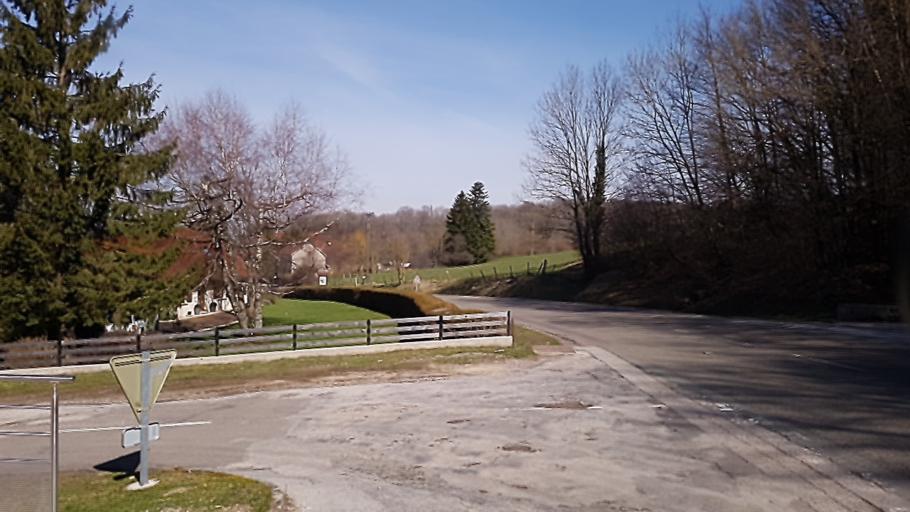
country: FR
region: Franche-Comte
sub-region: Departement du Jura
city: Champagnole
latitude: 46.7974
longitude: 5.8345
